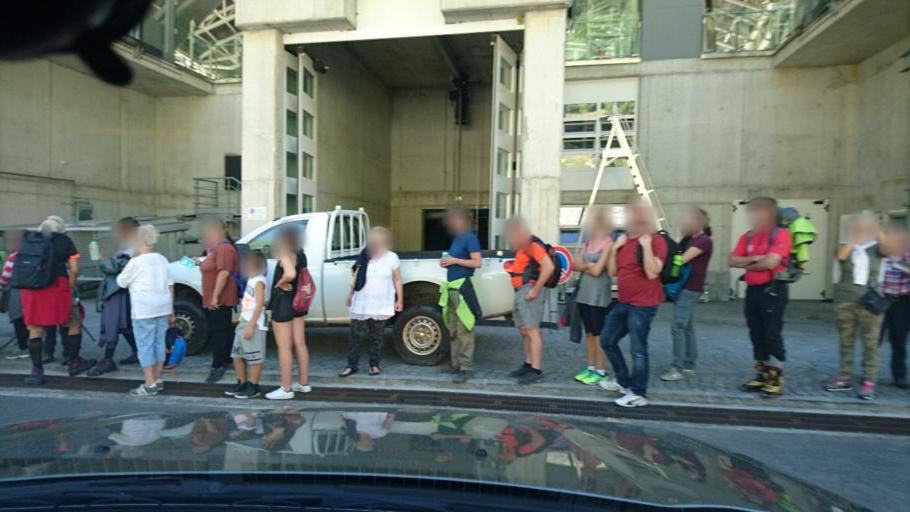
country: IT
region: Aosta Valley
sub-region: Valle d'Aosta
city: Courmayeur
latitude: 45.8161
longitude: 6.9560
